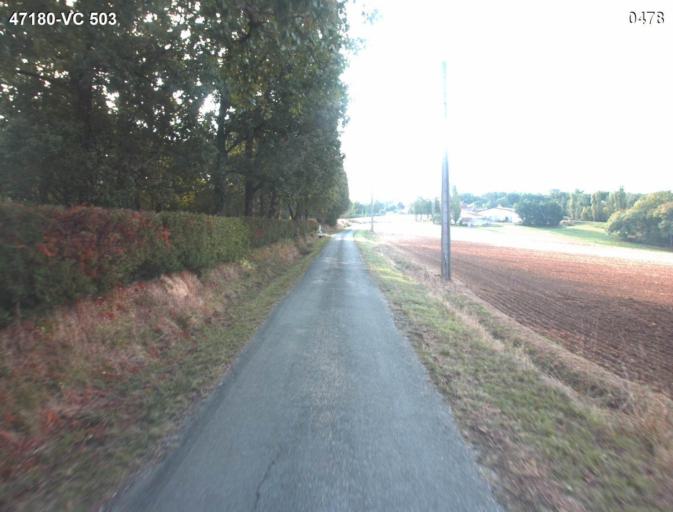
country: FR
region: Aquitaine
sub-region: Departement du Lot-et-Garonne
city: Port-Sainte-Marie
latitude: 44.1794
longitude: 0.4310
